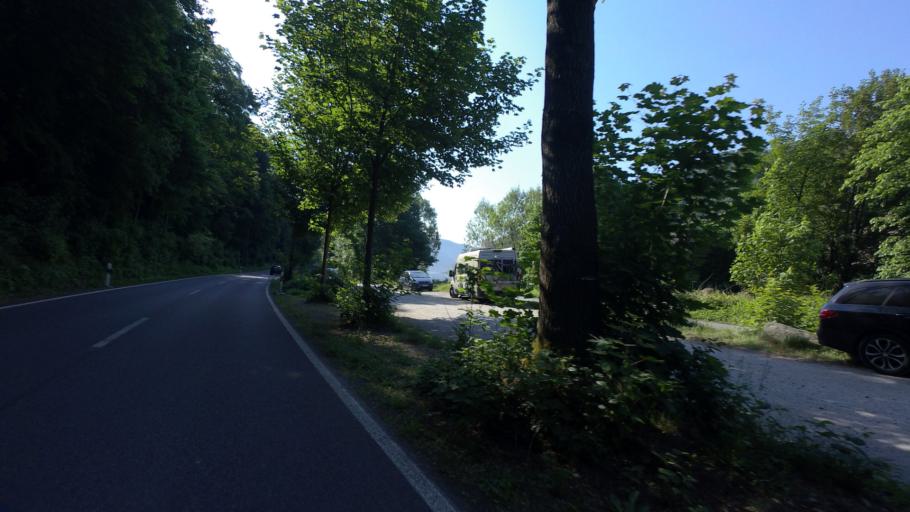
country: DE
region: Saxony
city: Bad Schandau
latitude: 50.9013
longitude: 14.2176
